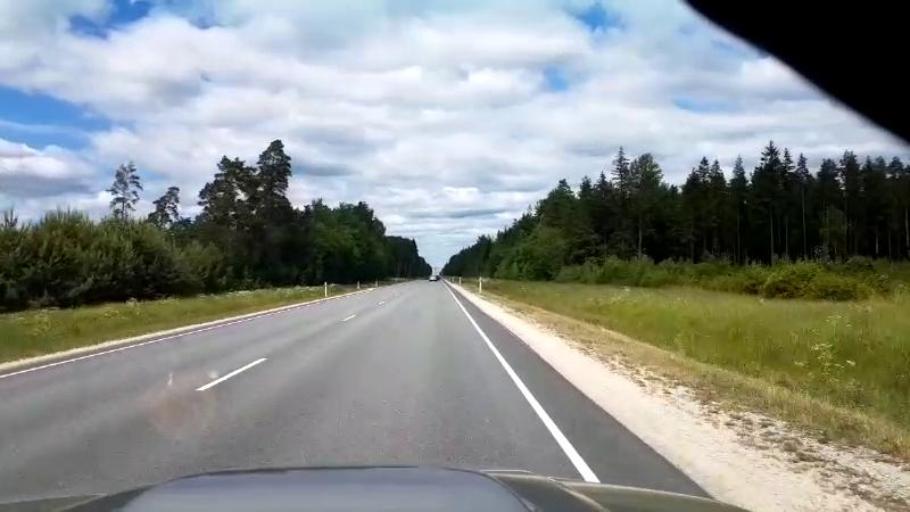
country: EE
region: Raplamaa
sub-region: Maerjamaa vald
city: Marjamaa
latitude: 58.7837
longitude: 24.4132
